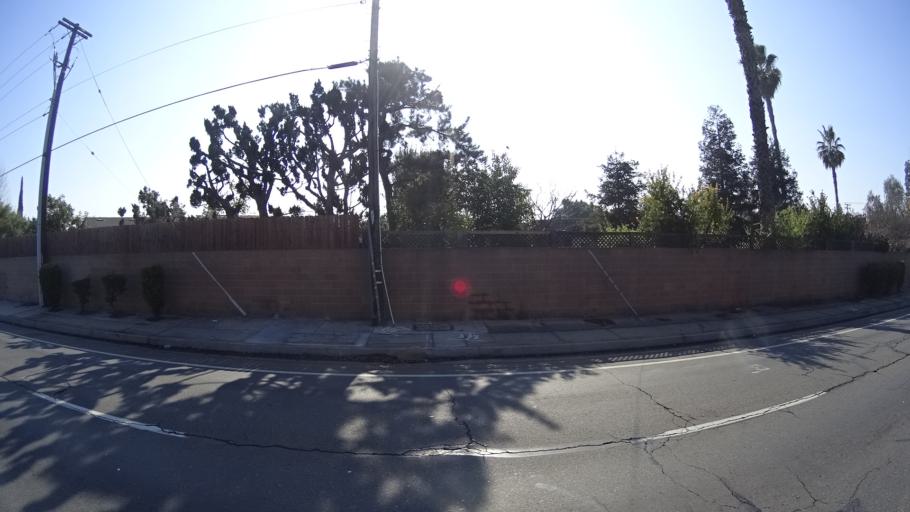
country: US
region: California
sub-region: Kern County
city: Greenacres
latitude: 35.3543
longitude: -119.0727
